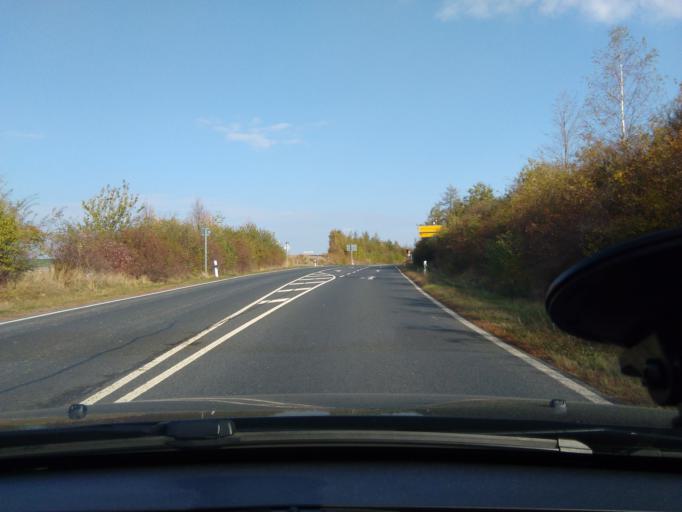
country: DE
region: Saxony
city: Meissen
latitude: 51.1642
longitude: 13.4438
